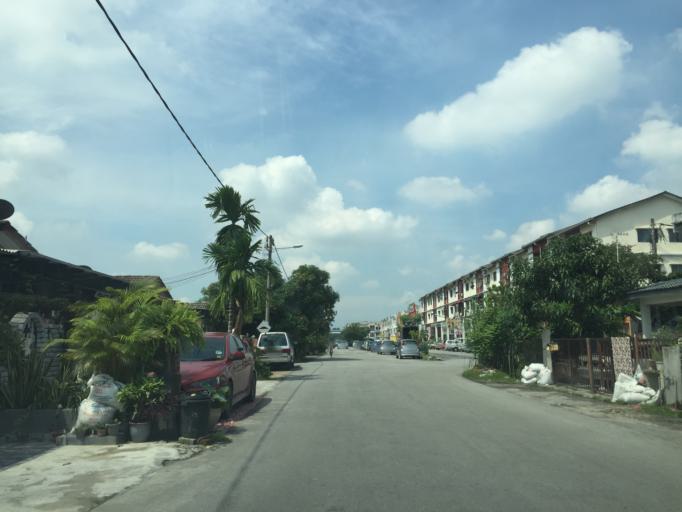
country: MY
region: Selangor
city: Klang
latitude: 3.0079
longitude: 101.4677
